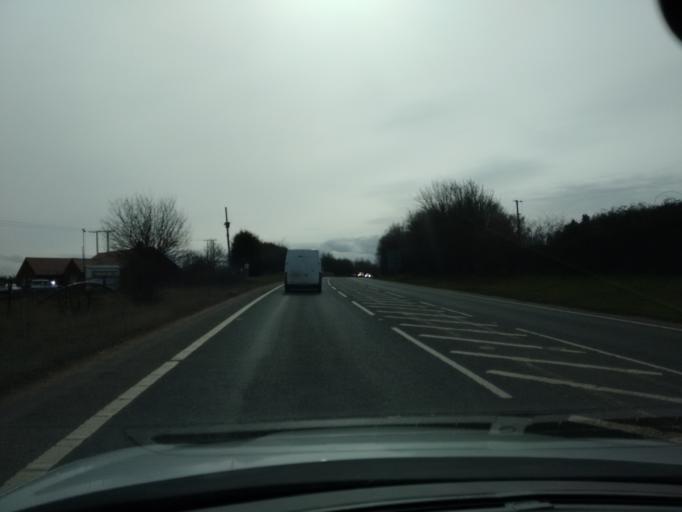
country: GB
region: England
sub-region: Worcestershire
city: Evesham
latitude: 52.1017
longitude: -1.9237
